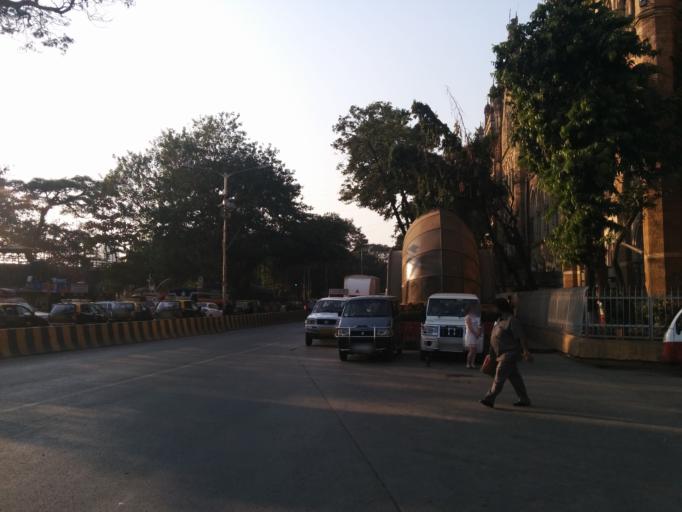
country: IN
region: Maharashtra
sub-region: Raigarh
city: Uran
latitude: 18.9402
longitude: 72.8345
